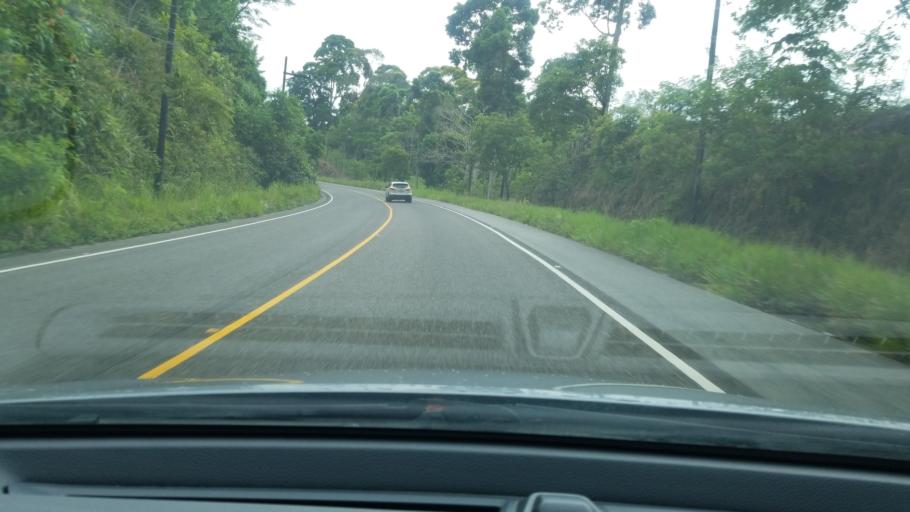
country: HN
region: Cortes
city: Potrerillos
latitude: 15.6093
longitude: -88.2898
